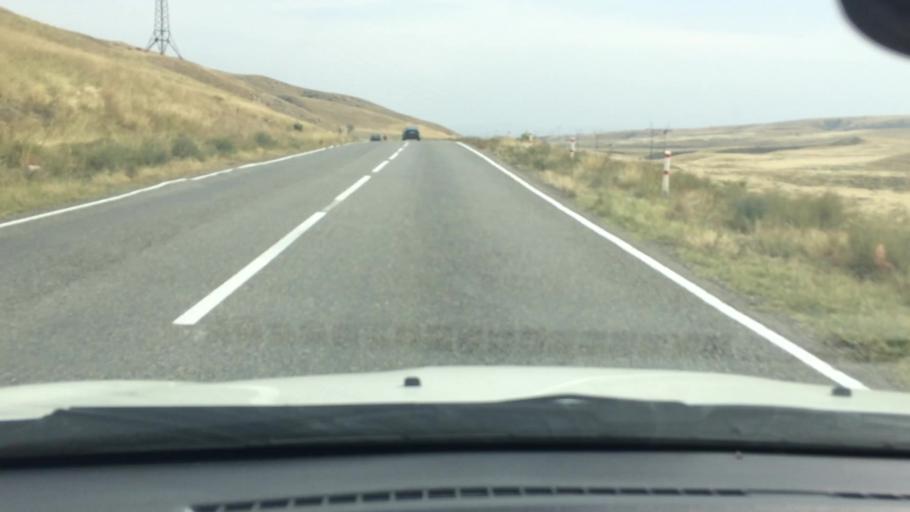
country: GE
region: Kvemo Kartli
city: Rust'avi
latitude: 41.5082
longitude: 44.9504
